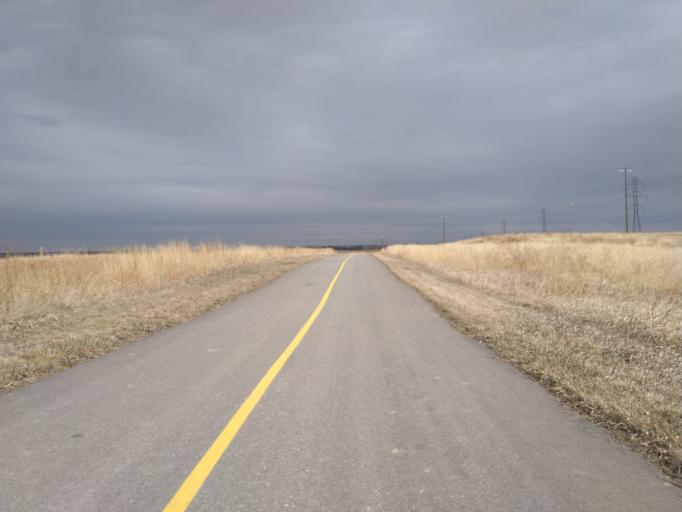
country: CA
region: Alberta
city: Airdrie
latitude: 51.1775
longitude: -114.0461
